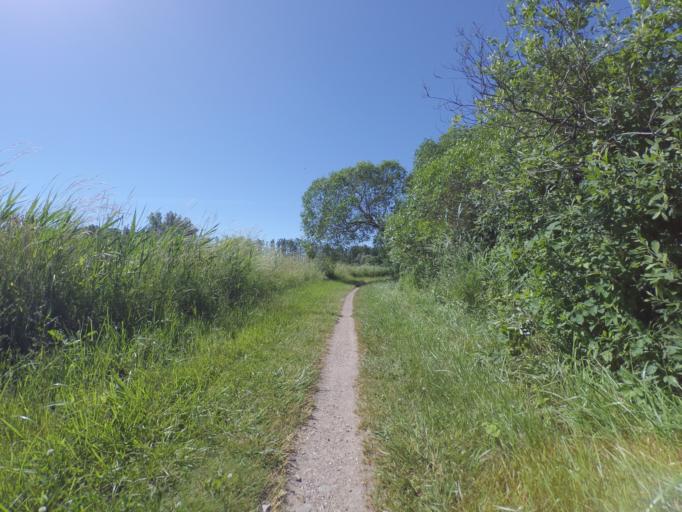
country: DE
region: Mecklenburg-Vorpommern
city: Plau am See
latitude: 53.5015
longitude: 12.3318
